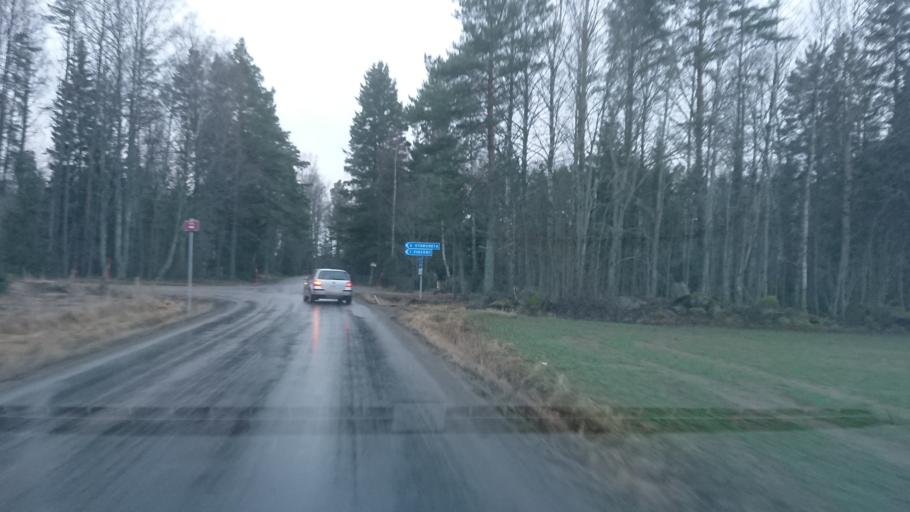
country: SE
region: Uppsala
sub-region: Osthammars Kommun
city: Bjorklinge
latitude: 59.9795
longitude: 17.5954
